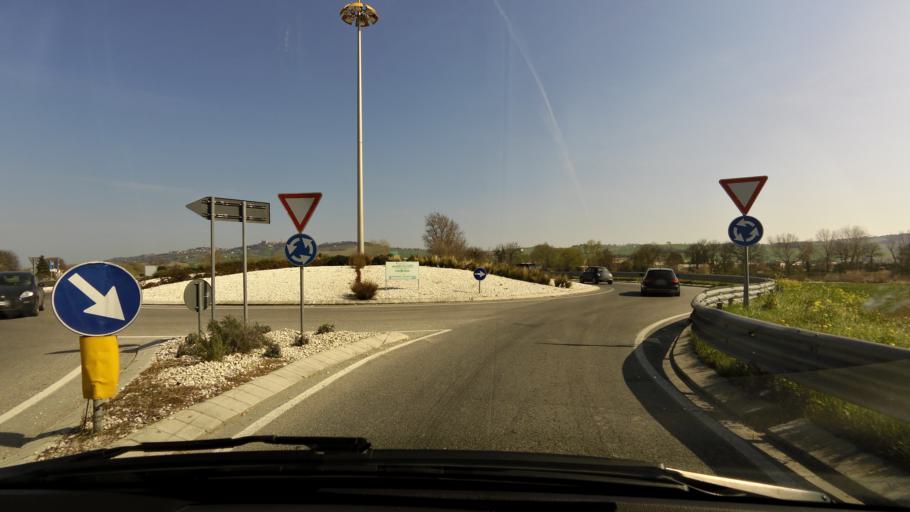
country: IT
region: The Marches
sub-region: Provincia di Macerata
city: Montelupone
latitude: 43.3750
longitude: 13.5760
